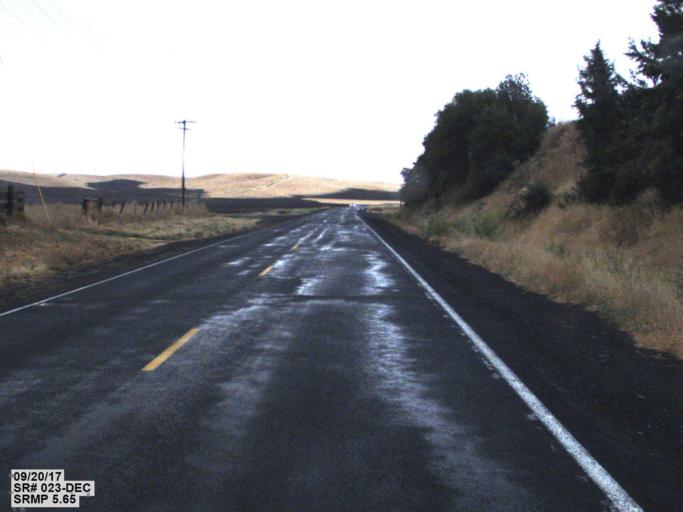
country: US
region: Washington
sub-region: Whitman County
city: Colfax
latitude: 47.0099
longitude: -117.4680
